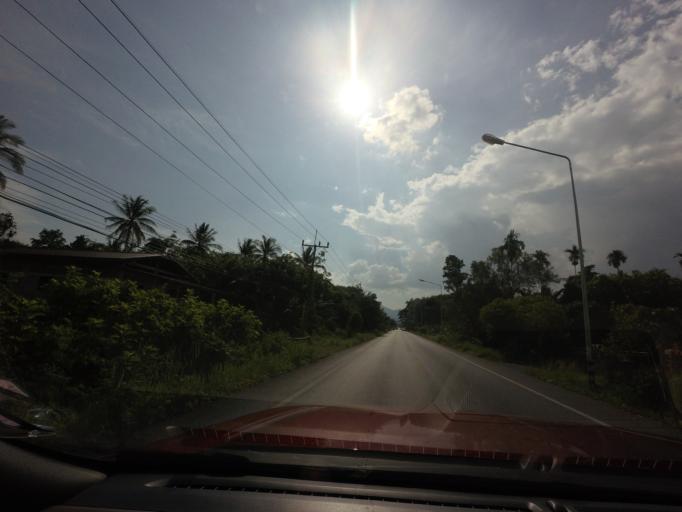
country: TH
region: Yala
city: Yala
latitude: 6.5635
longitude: 101.2141
